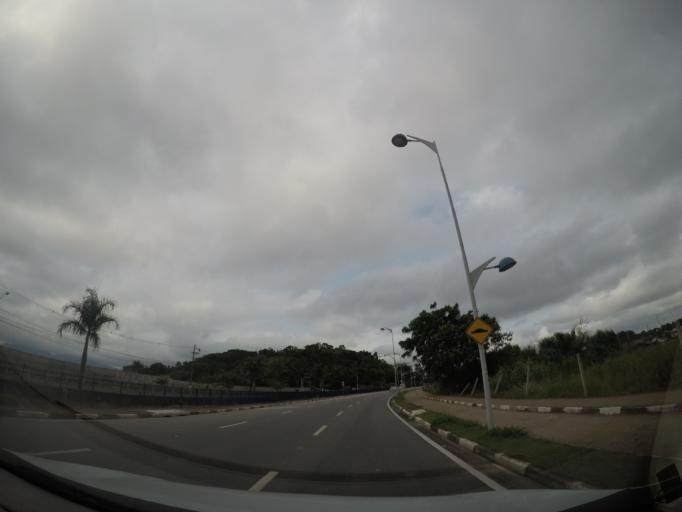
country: BR
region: Sao Paulo
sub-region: Aruja
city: Aruja
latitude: -23.4040
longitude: -46.3641
